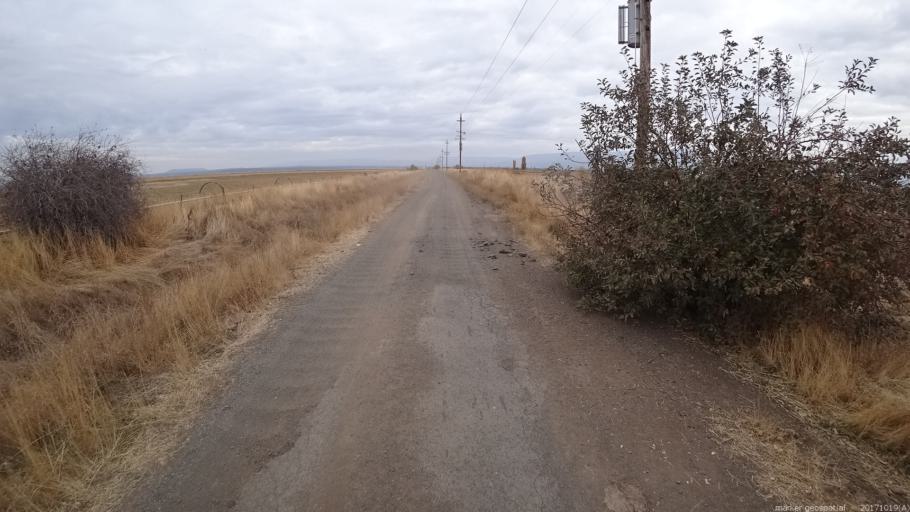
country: US
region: California
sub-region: Shasta County
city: Burney
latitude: 41.0667
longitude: -121.3891
